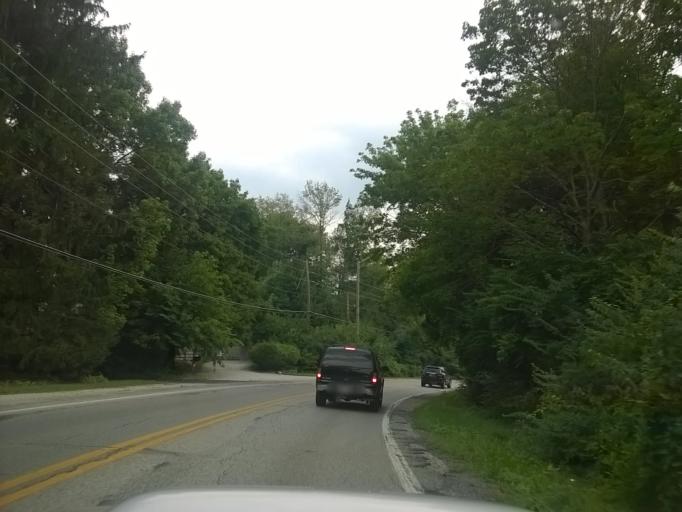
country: US
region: Indiana
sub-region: Marion County
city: Meridian Hills
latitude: 39.8969
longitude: -86.1364
